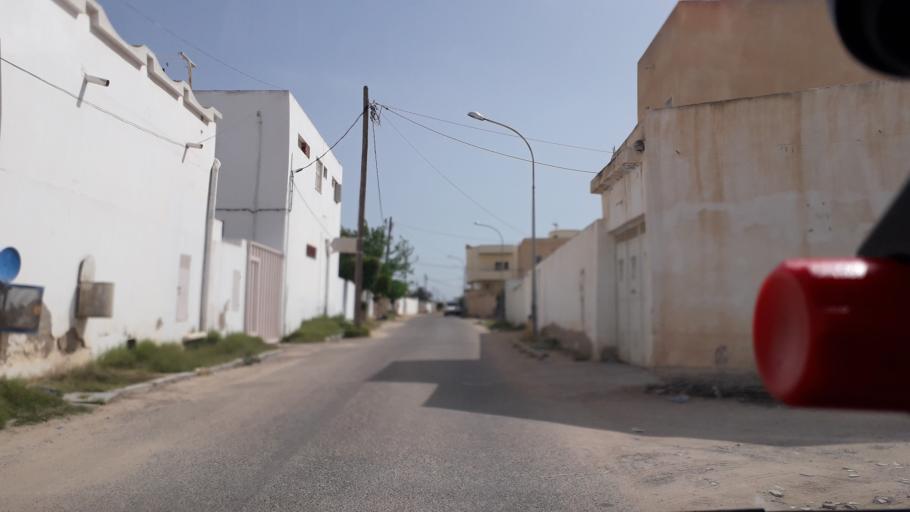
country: TN
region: Safaqis
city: Al Qarmadah
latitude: 34.7967
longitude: 10.7732
